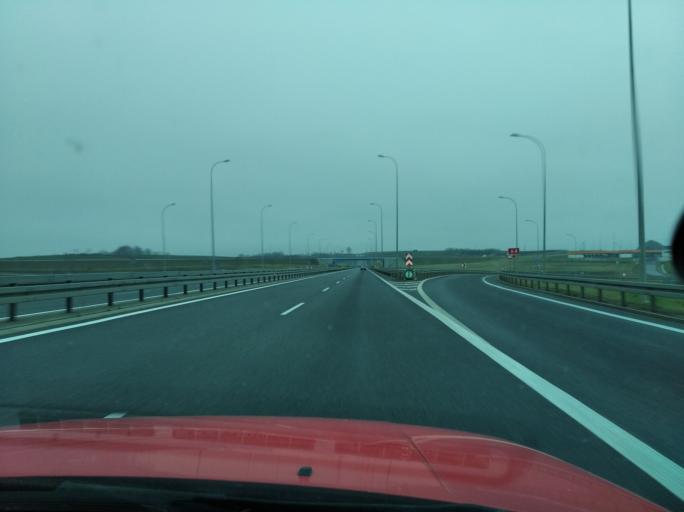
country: PL
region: Subcarpathian Voivodeship
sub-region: Powiat jaroslawski
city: Wierzbna
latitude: 50.0368
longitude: 22.5795
